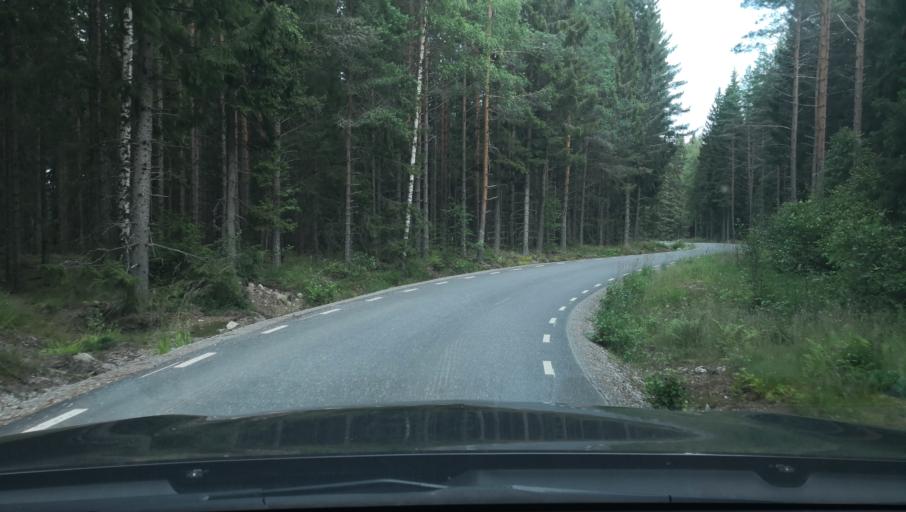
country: SE
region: Vaestmanland
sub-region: Surahammars Kommun
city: Surahammar
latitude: 59.6692
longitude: 16.1369
